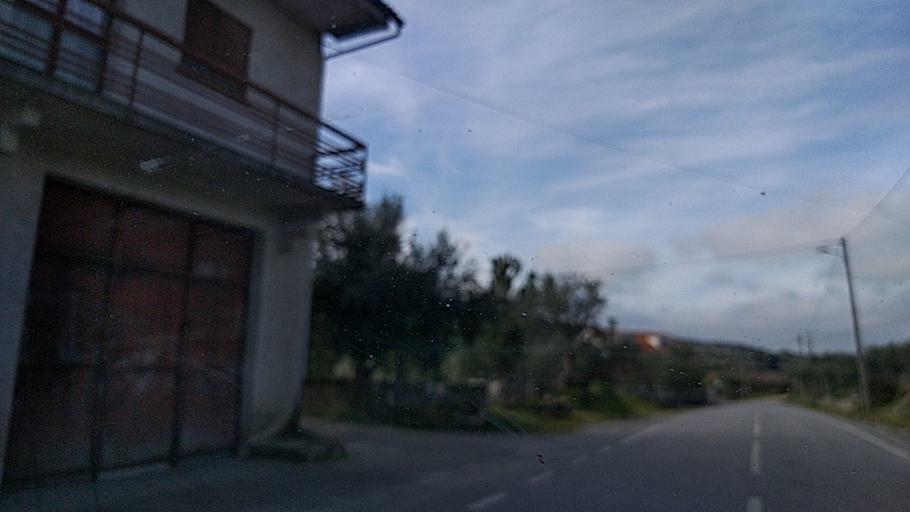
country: PT
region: Guarda
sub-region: Fornos de Algodres
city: Fornos de Algodres
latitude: 40.7034
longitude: -7.5581
